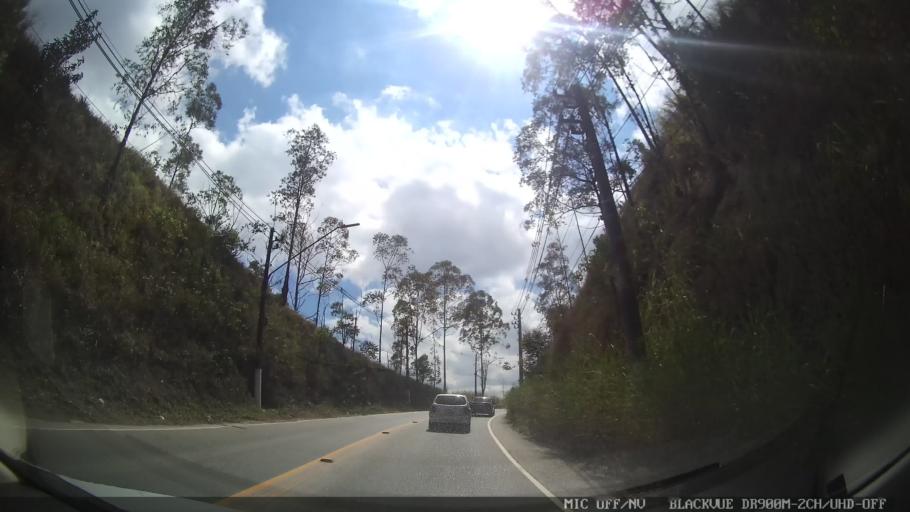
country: BR
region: Sao Paulo
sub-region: Caieiras
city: Caieiras
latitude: -23.4079
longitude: -46.7762
